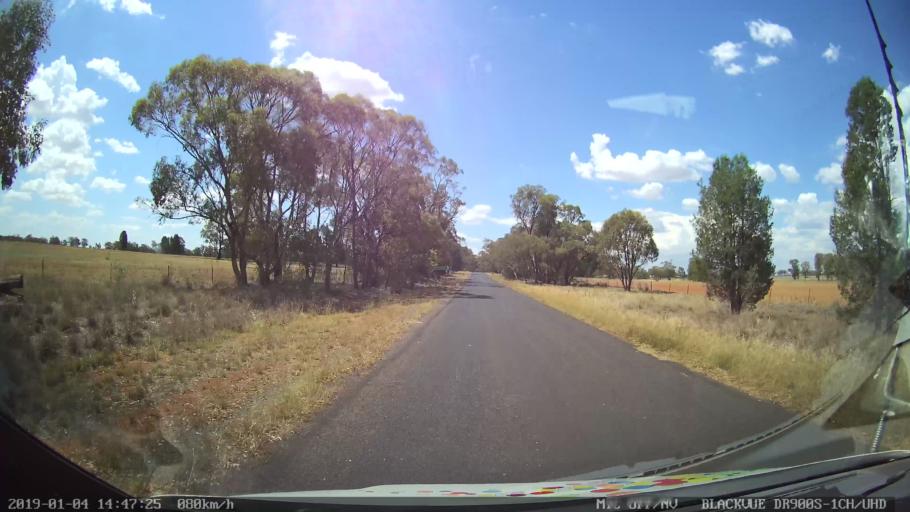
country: AU
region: New South Wales
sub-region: Dubbo Municipality
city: Dubbo
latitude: -32.0693
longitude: 148.6602
